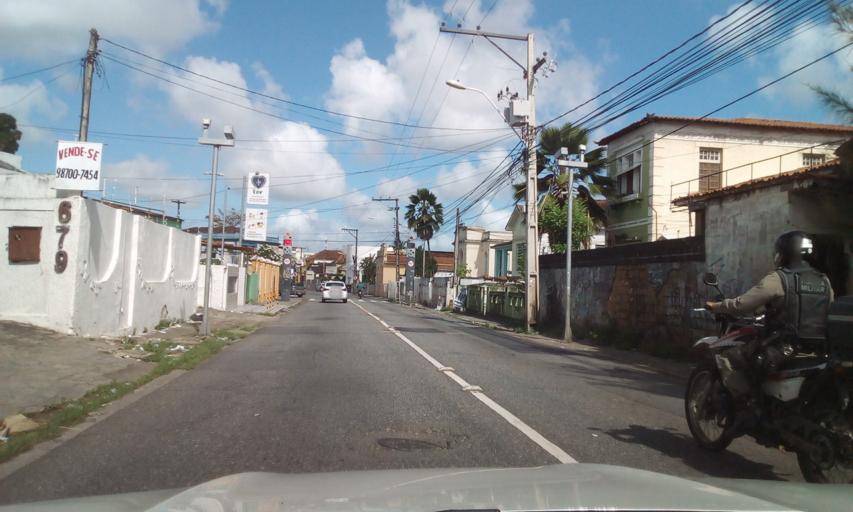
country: BR
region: Paraiba
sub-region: Joao Pessoa
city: Joao Pessoa
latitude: -7.1286
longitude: -34.8840
